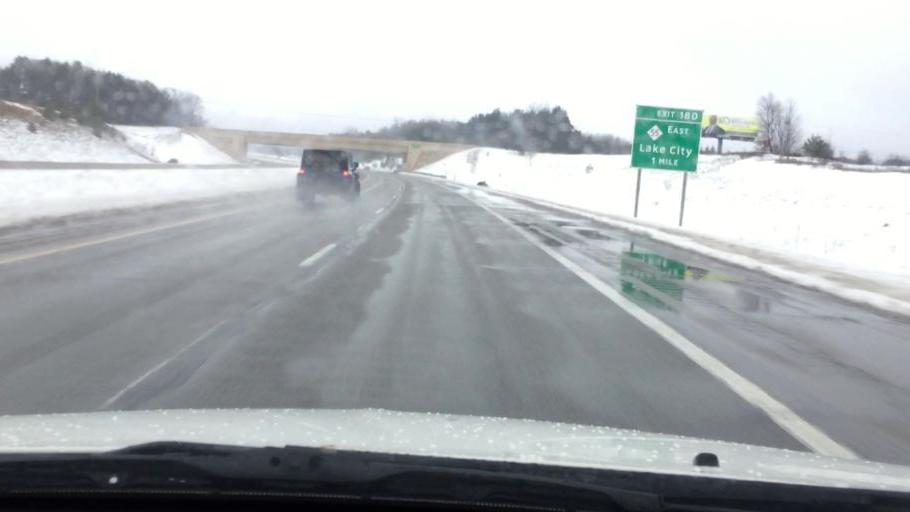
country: US
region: Michigan
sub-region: Wexford County
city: Cadillac
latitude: 44.2689
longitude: -85.3885
